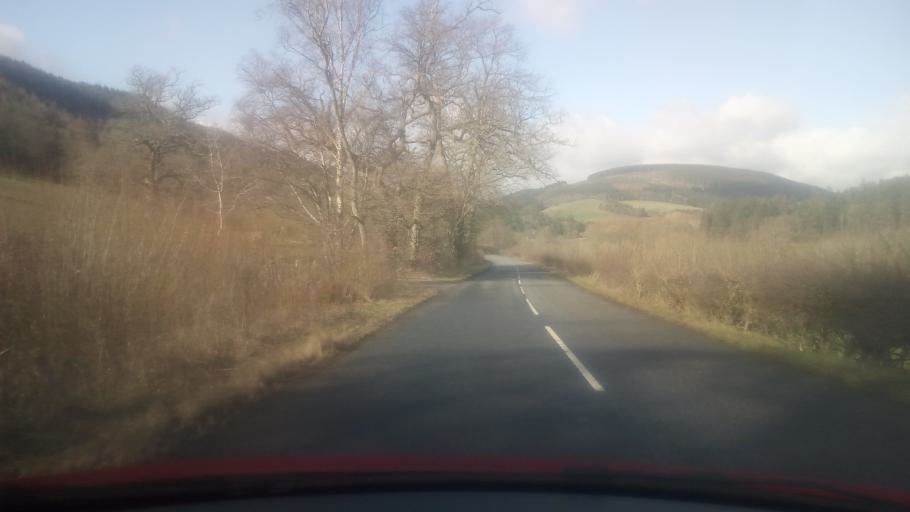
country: GB
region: Scotland
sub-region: The Scottish Borders
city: Selkirk
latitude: 55.5815
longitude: -2.8443
